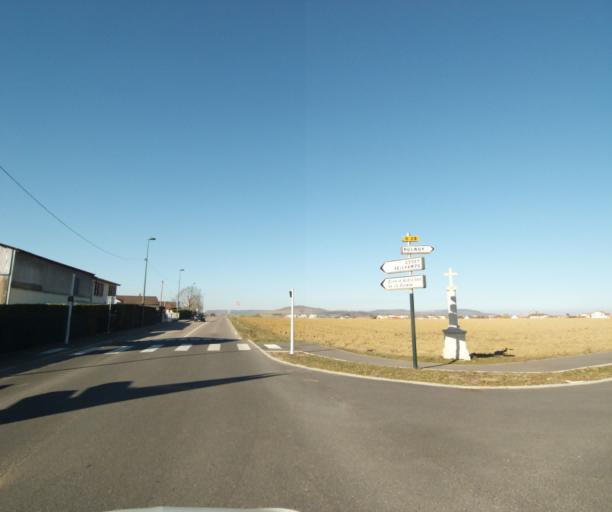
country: FR
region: Lorraine
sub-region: Departement de Meurthe-et-Moselle
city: Saulxures-les-Nancy
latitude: 48.6935
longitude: 6.2507
